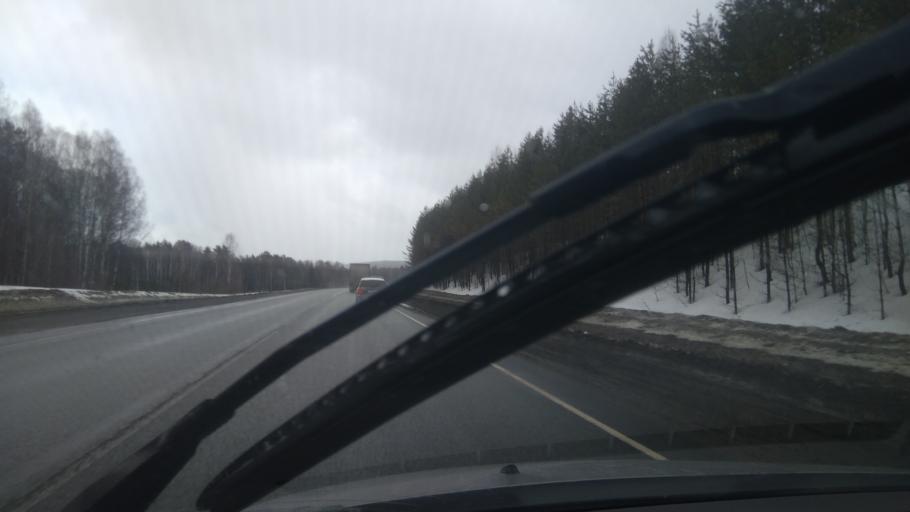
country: RU
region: Sverdlovsk
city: Ufimskiy
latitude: 56.7864
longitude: 58.3868
